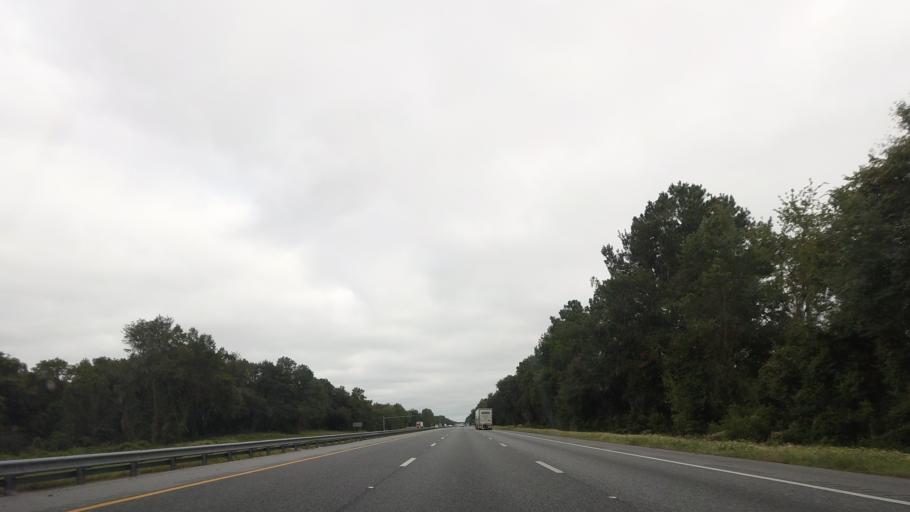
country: US
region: Florida
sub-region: Hamilton County
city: Jasper
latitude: 30.4037
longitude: -82.8877
